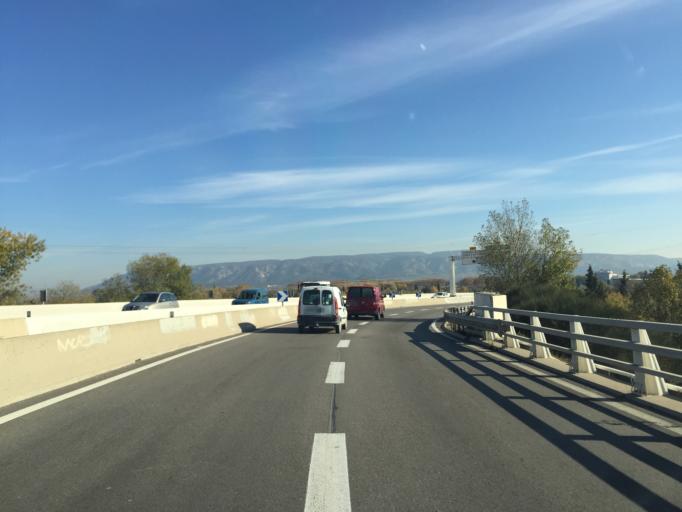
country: FR
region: Provence-Alpes-Cote d'Azur
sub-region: Departement du Vaucluse
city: Cavaillon
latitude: 43.8230
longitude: 5.0293
